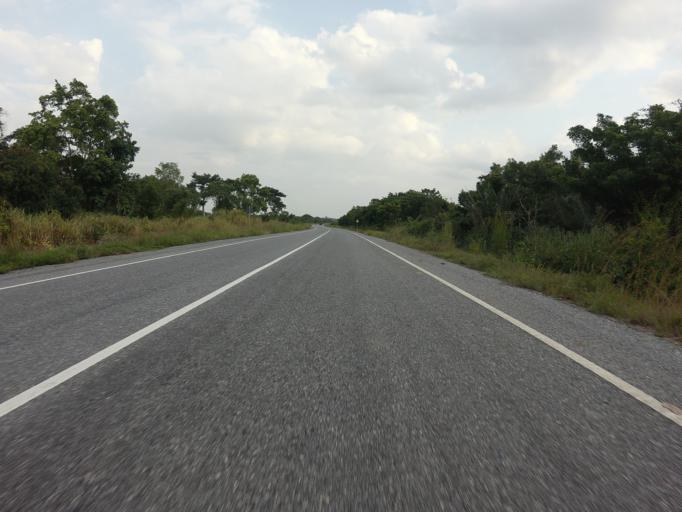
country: GH
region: Volta
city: Ho
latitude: 6.3650
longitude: 0.5353
